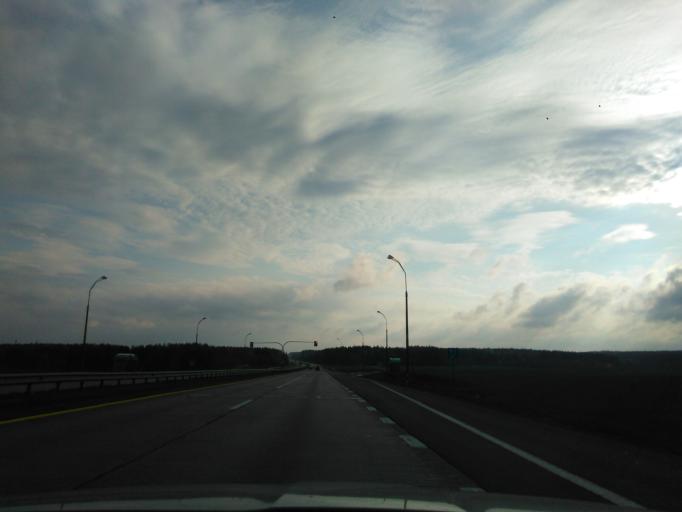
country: BY
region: Minsk
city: Astrashytski Haradok
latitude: 54.0957
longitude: 27.7812
